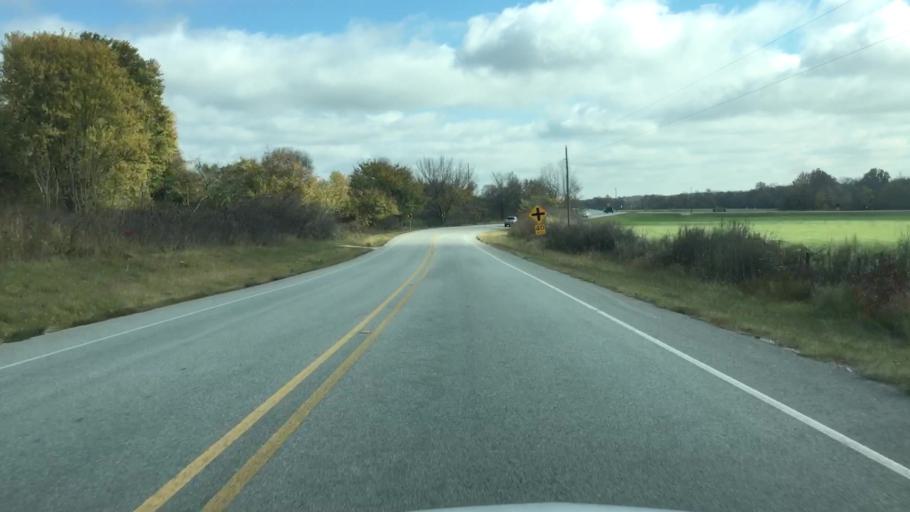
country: US
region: Arkansas
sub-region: Benton County
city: Centerton
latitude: 36.3016
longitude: -94.3106
